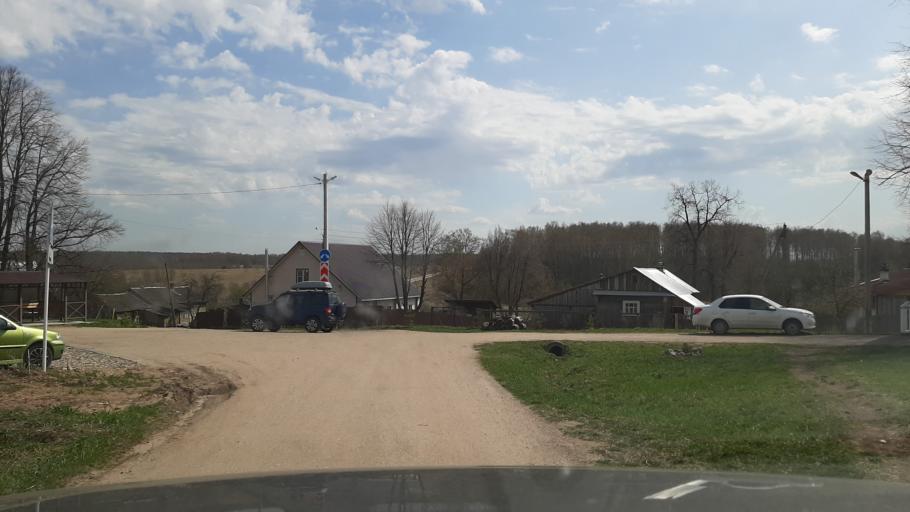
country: RU
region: Ivanovo
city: Furmanov
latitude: 57.3168
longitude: 41.1615
